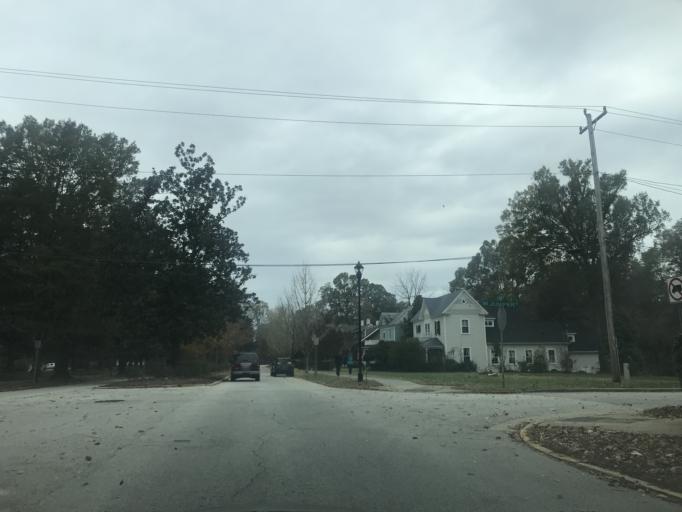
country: US
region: North Carolina
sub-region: Wake County
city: Wake Forest
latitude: 35.9856
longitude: -78.5078
